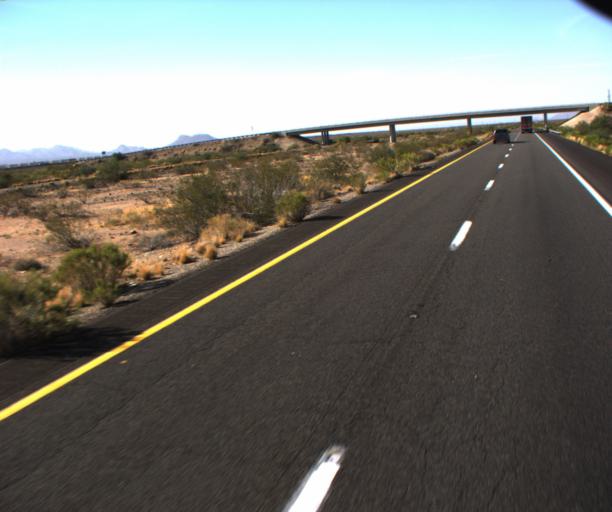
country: US
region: Arizona
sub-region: Mohave County
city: Kingman
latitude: 35.0355
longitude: -114.1304
